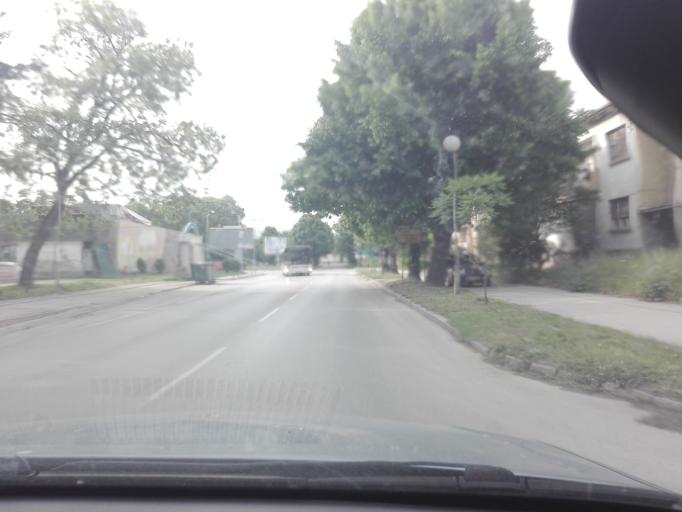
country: MK
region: Bitola
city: Bitola
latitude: 41.0228
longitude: 21.3396
